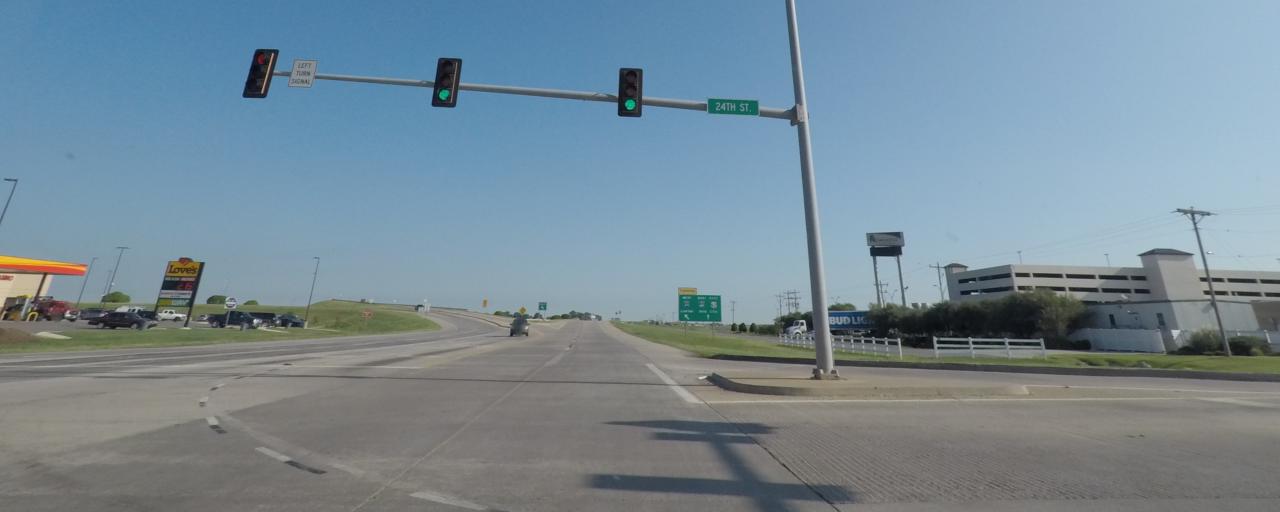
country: US
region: Oklahoma
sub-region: McClain County
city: Newcastle
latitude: 35.2764
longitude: -97.6001
